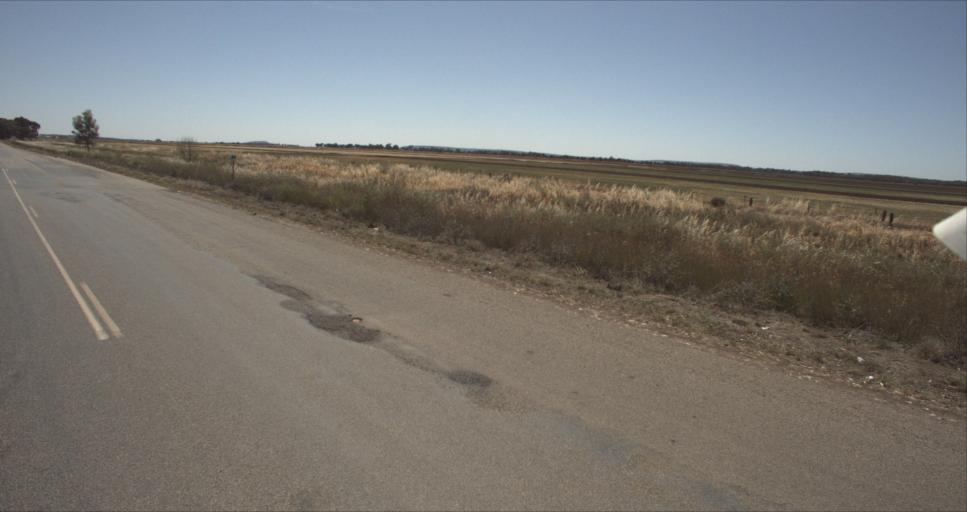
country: AU
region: New South Wales
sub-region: Leeton
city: Leeton
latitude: -34.4980
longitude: 146.2874
